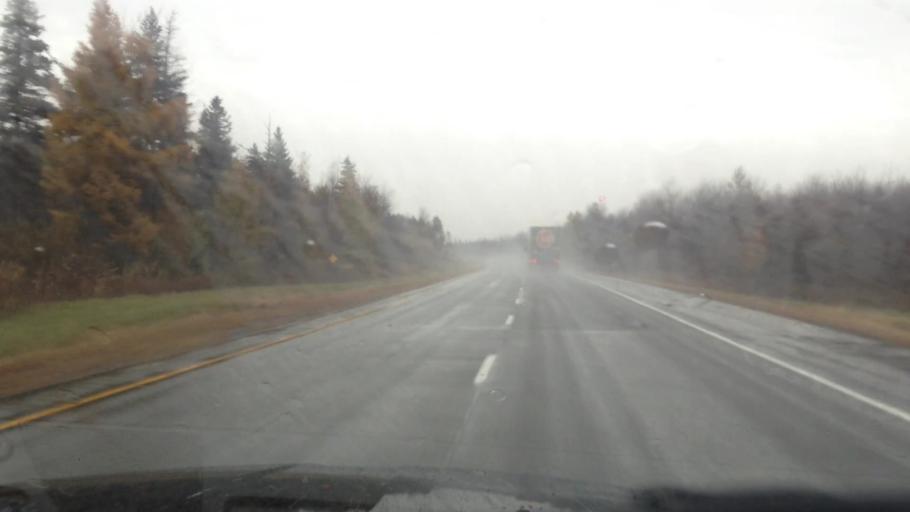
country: CA
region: Ontario
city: Casselman
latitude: 45.3121
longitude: -75.2154
